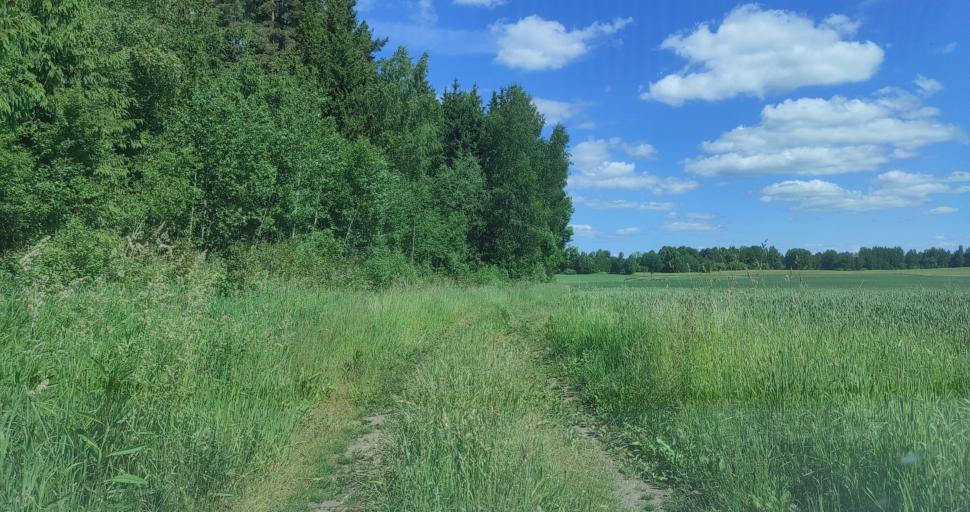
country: LV
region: Aizpute
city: Aizpute
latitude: 56.8533
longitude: 21.7256
